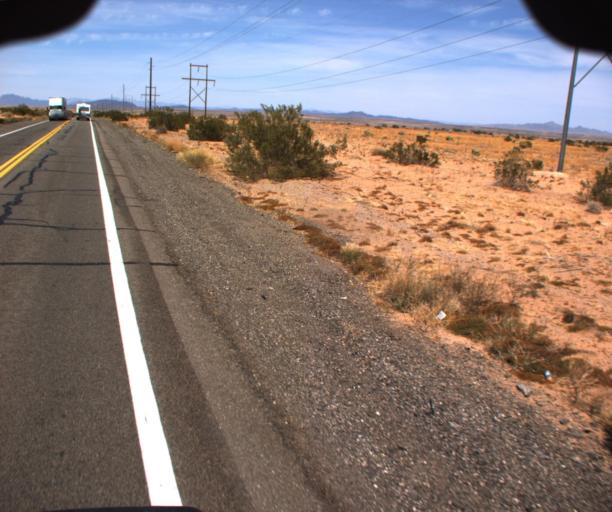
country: US
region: Arizona
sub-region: La Paz County
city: Parker
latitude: 33.9454
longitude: -114.2169
